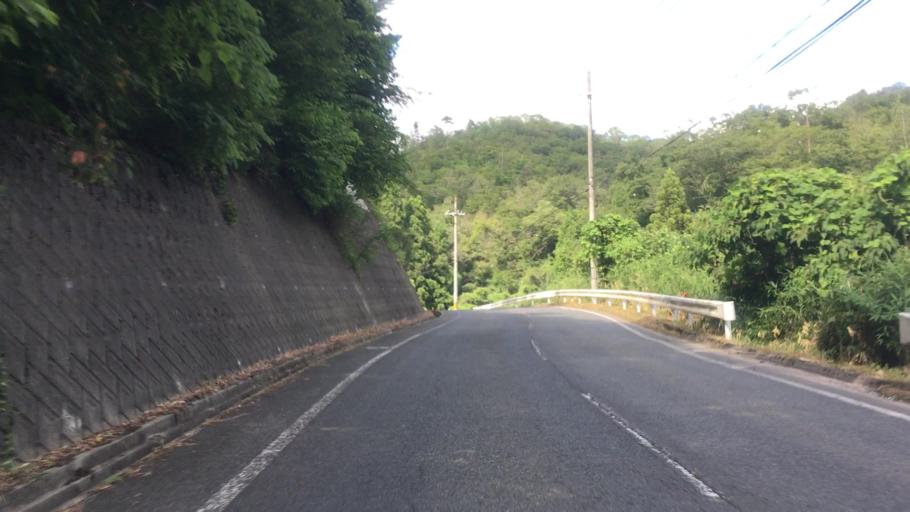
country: JP
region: Hyogo
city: Toyooka
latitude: 35.5103
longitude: 134.7799
